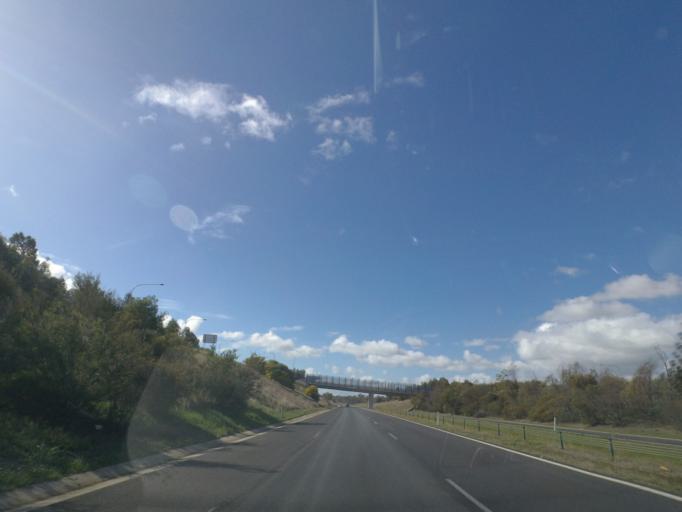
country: AU
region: New South Wales
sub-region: Albury Municipality
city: Lavington
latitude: -36.0534
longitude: 146.9574
